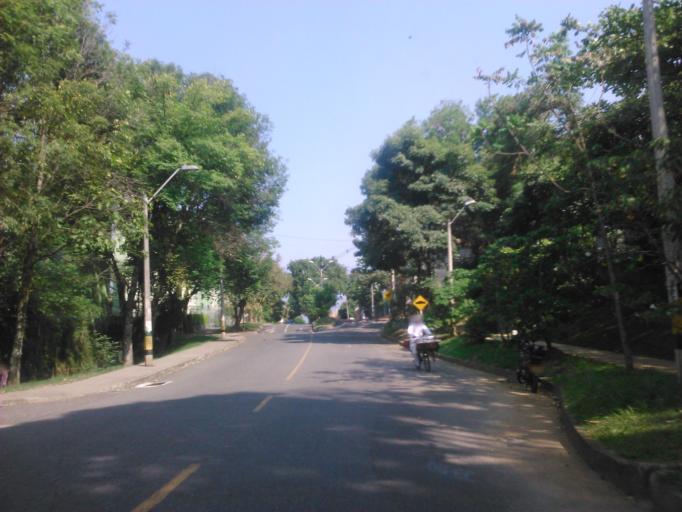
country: CO
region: Antioquia
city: Medellin
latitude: 6.2512
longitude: -75.6138
